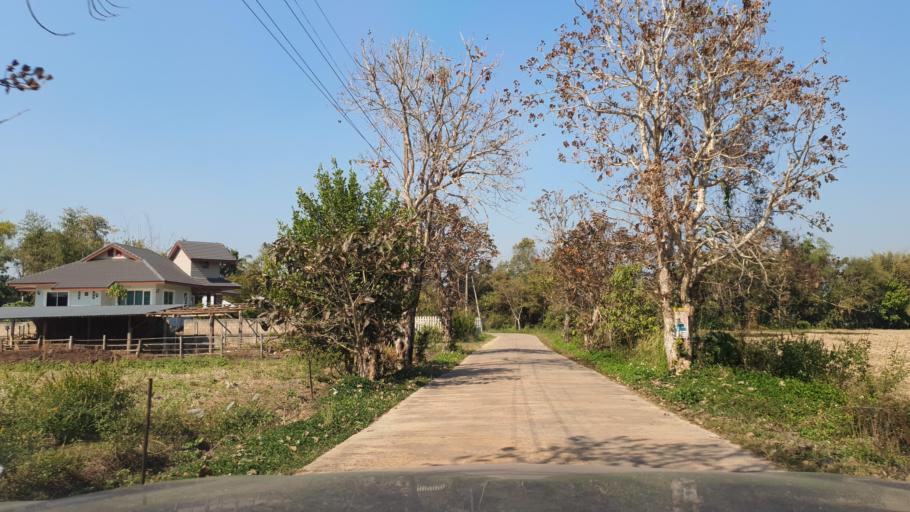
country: TH
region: Chiang Rai
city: Mae Lao
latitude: 19.7976
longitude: 99.7023
